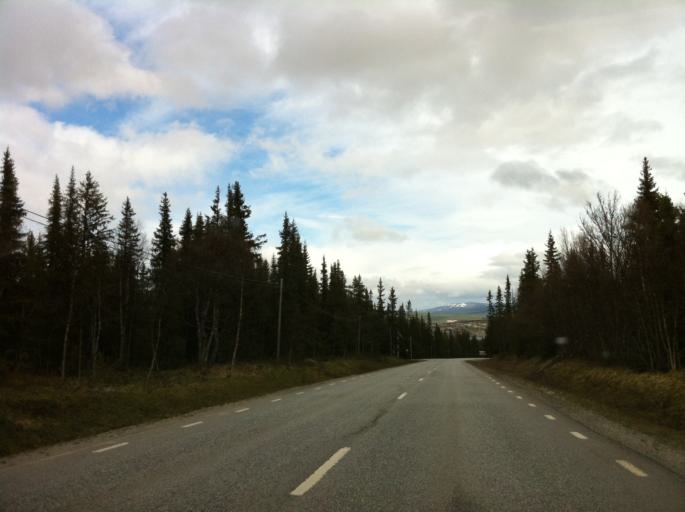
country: NO
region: Hedmark
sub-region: Engerdal
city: Engerdal
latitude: 62.5371
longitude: 12.4206
